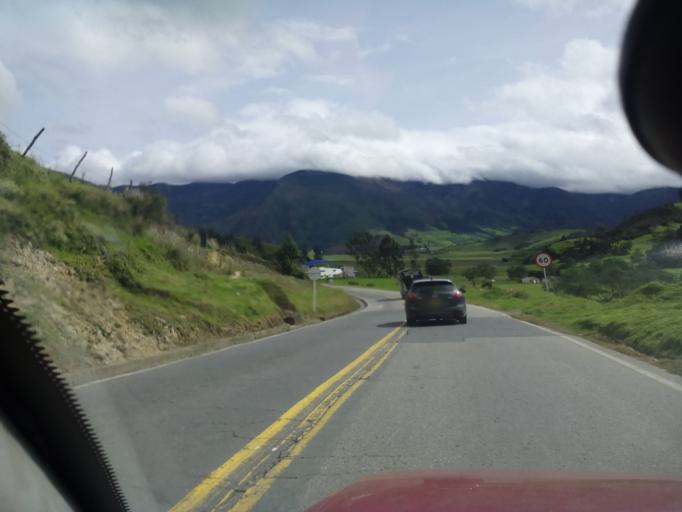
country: CO
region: Boyaca
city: Combita
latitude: 5.6882
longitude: -73.3668
